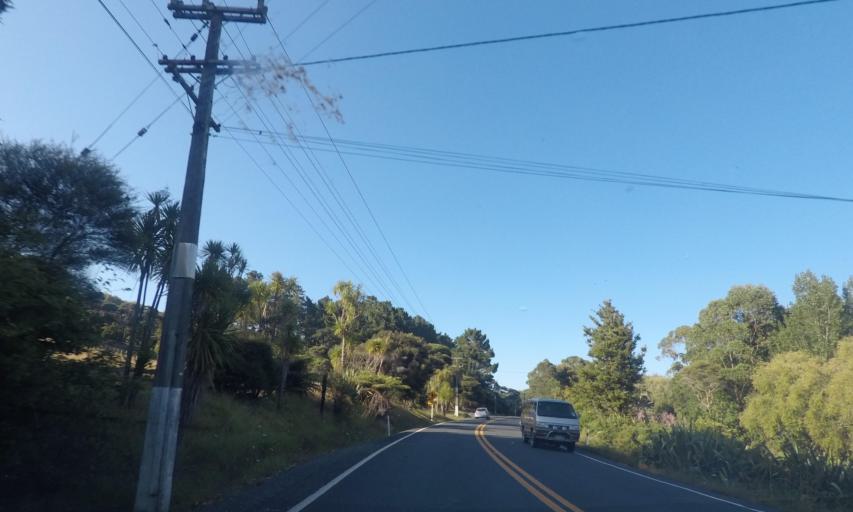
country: NZ
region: Auckland
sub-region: Auckland
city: Muriwai Beach
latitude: -36.7883
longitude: 174.4757
